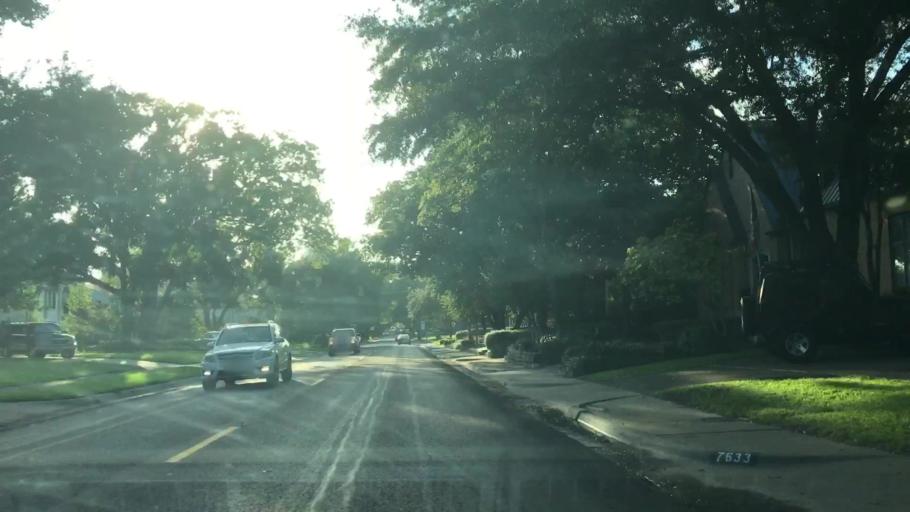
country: US
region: Texas
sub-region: Dallas County
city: University Park
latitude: 32.8571
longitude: -96.7753
